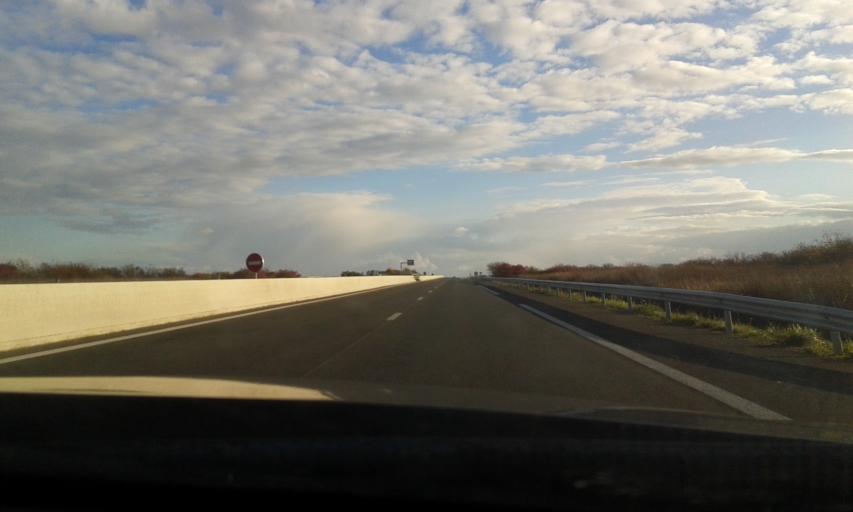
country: FR
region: Centre
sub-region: Departement d'Eure-et-Loir
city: Bailleau-l'Eveque
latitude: 48.5632
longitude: 1.4404
